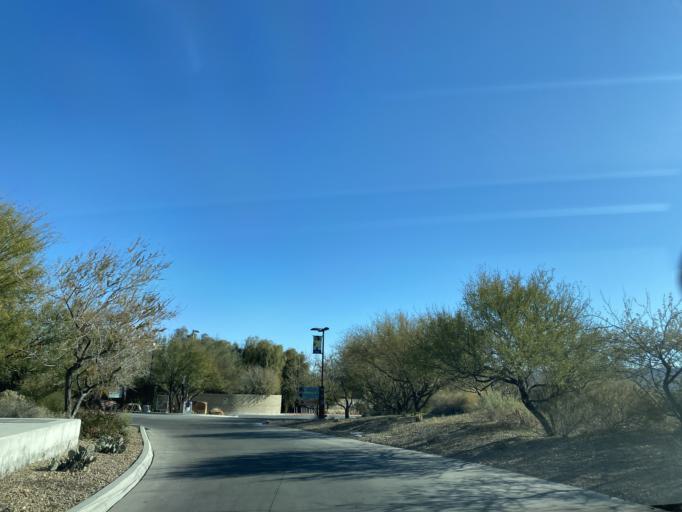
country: US
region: Nevada
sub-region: Clark County
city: Las Vegas
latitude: 36.1699
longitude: -115.1913
